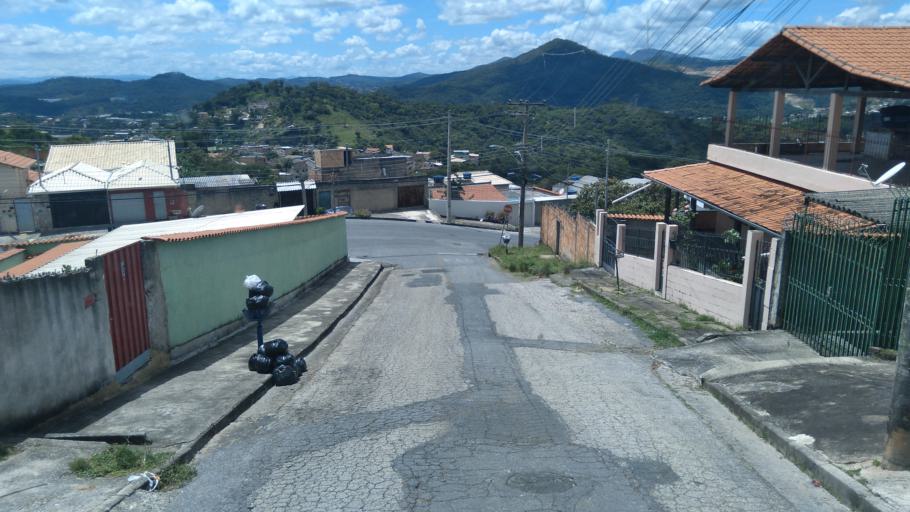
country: BR
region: Minas Gerais
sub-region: Belo Horizonte
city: Belo Horizonte
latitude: -19.8552
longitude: -43.8826
